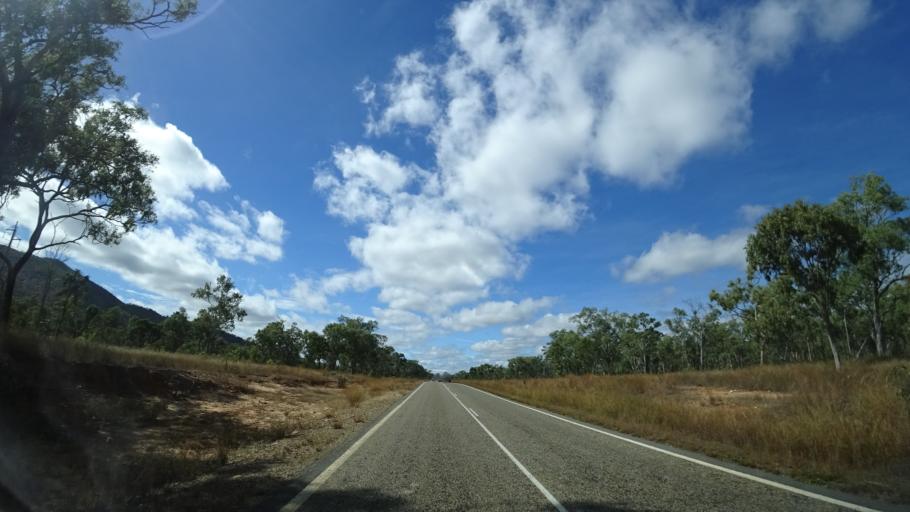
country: AU
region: Queensland
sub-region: Cairns
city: Port Douglas
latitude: -16.4861
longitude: 144.9065
